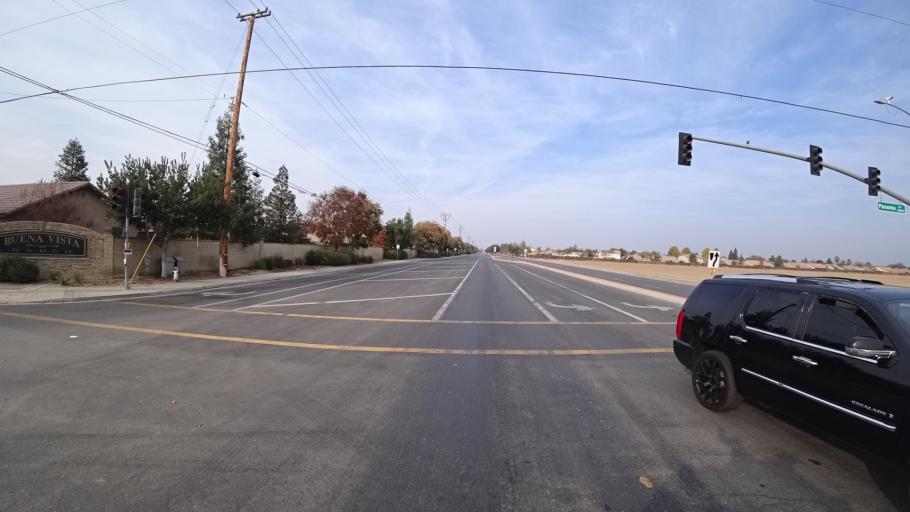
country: US
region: California
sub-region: Kern County
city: Greenacres
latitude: 35.2963
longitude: -119.1283
